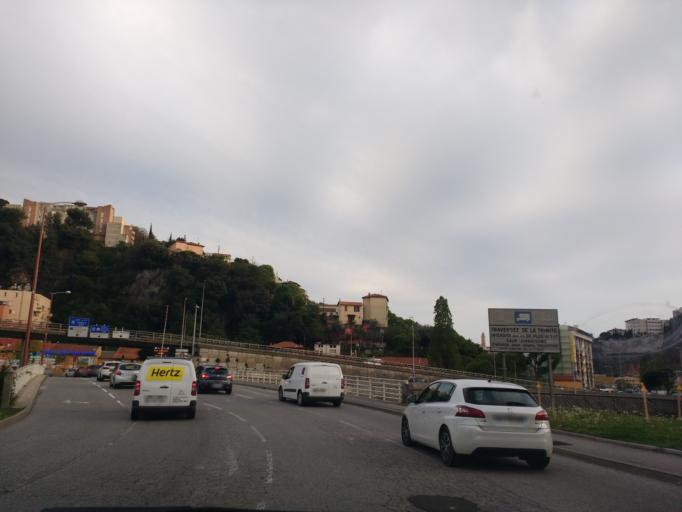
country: FR
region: Provence-Alpes-Cote d'Azur
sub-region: Departement des Alpes-Maritimes
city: Saint-Andre-de-la-Roche
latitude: 43.7318
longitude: 7.2853
